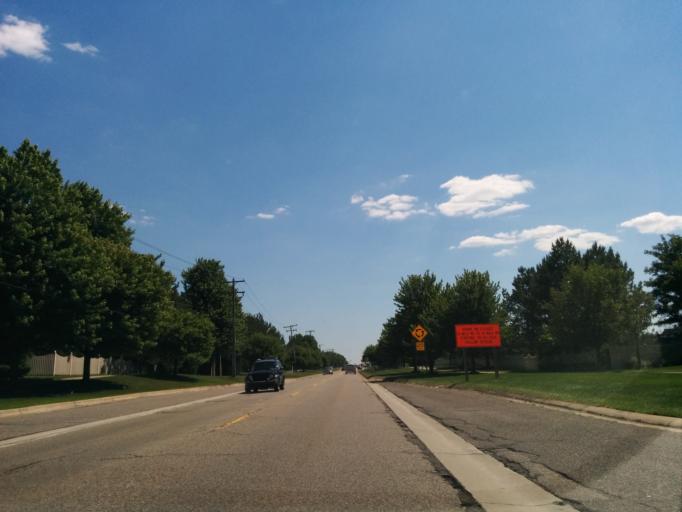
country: US
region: Michigan
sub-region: Oakland County
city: West Bloomfield Township
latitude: 42.5328
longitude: -83.3799
